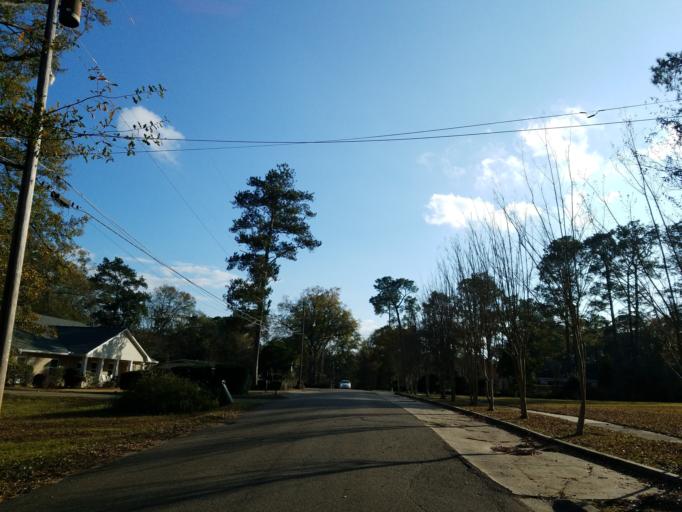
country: US
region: Mississippi
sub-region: Lamar County
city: West Hattiesburg
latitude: 31.3201
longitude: -89.3437
